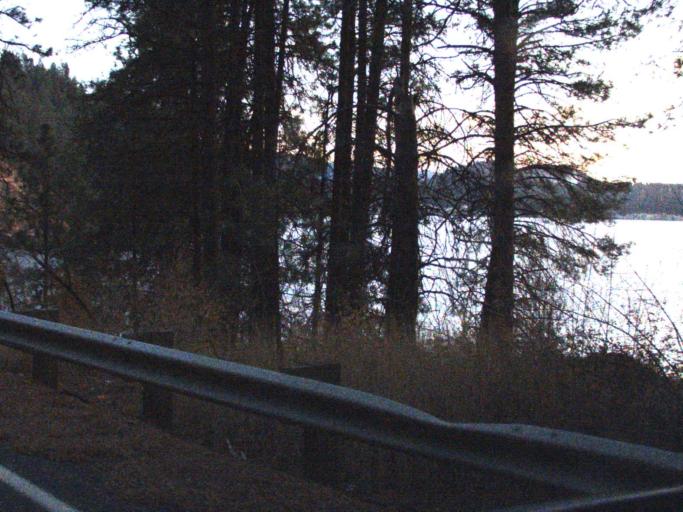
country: US
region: Washington
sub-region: Stevens County
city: Kettle Falls
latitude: 48.6481
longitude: -118.0819
